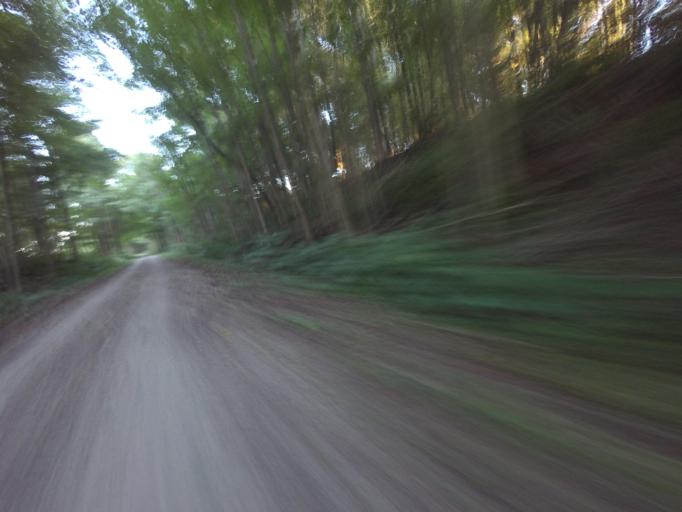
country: CA
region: Ontario
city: Goderich
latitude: 43.7472
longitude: -81.6412
